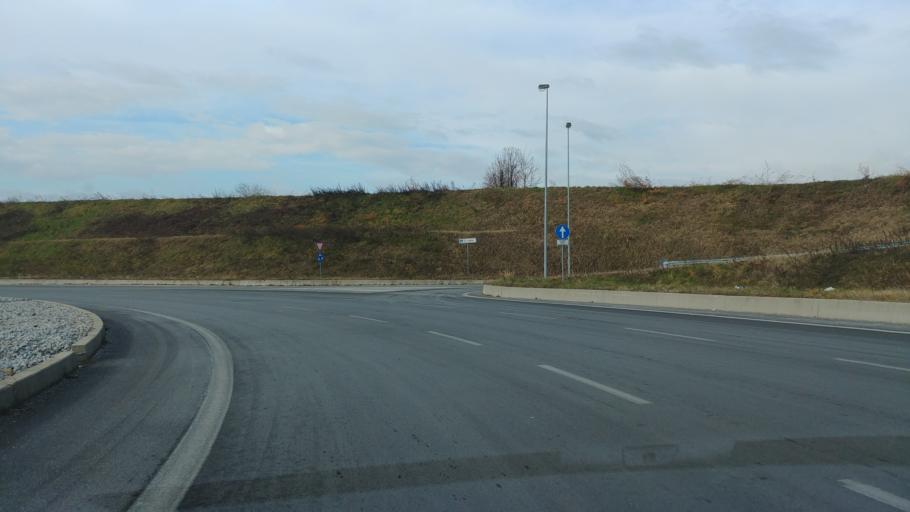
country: IT
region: Piedmont
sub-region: Provincia di Cuneo
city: Cuneo
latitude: 44.3884
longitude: 7.5204
